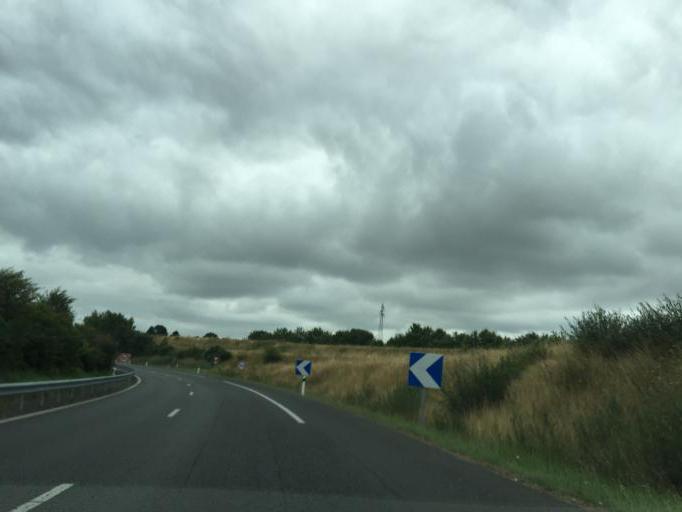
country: FR
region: Brittany
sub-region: Departement d'Ille-et-Vilaine
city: Cesson-Sevigne
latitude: 48.1143
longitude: -1.5707
